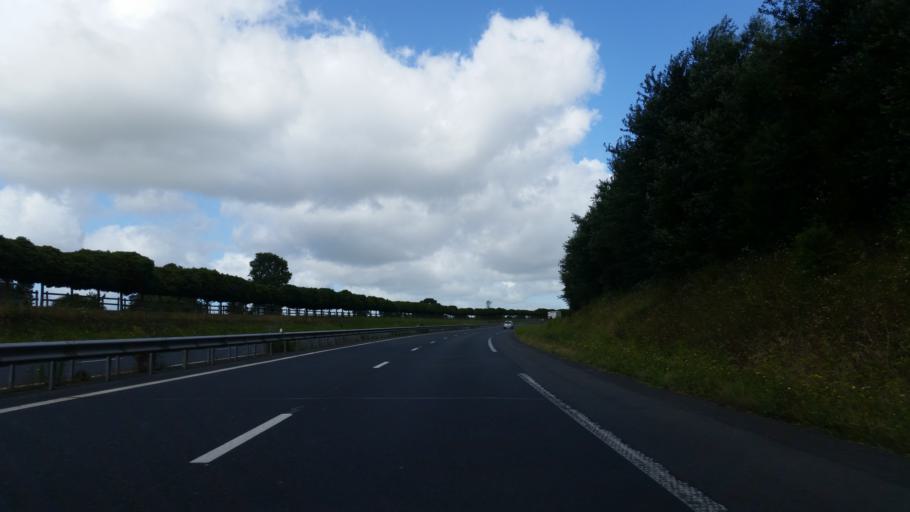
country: FR
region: Lower Normandy
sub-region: Departement du Calvados
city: Grandcamp-Maisy
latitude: 49.3390
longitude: -1.0120
